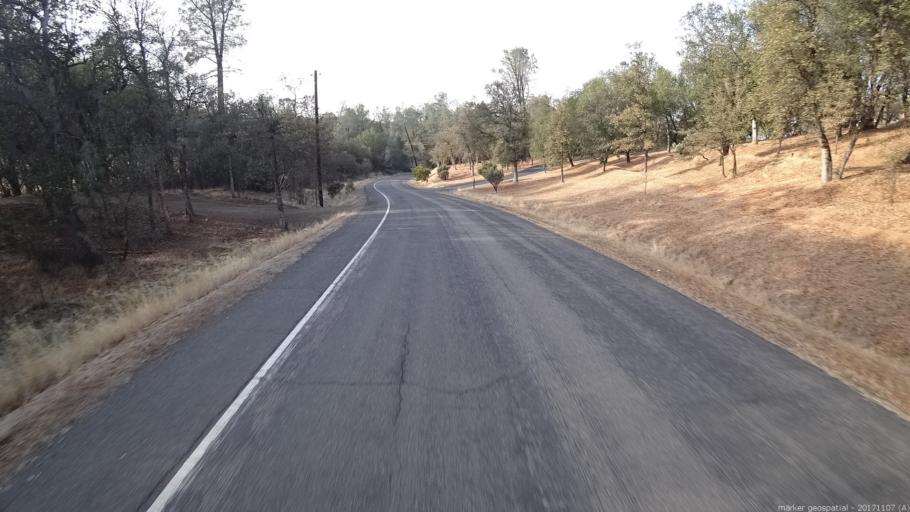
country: US
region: California
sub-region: Shasta County
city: Shasta
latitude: 40.5172
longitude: -122.4607
